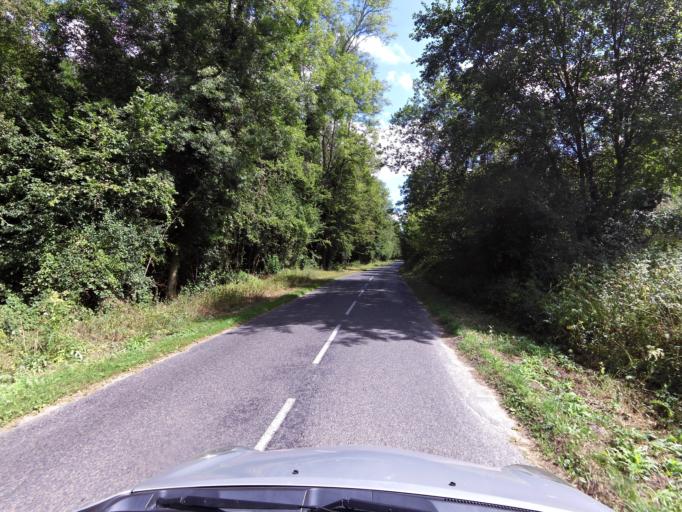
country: FR
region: Picardie
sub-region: Departement de l'Aisne
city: Villers-Cotterets
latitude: 49.2545
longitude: 3.1714
